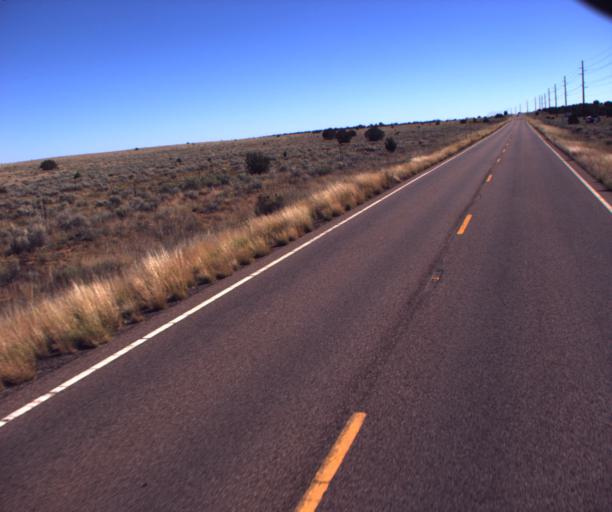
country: US
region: Arizona
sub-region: Navajo County
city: Taylor
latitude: 34.4832
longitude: -110.2740
